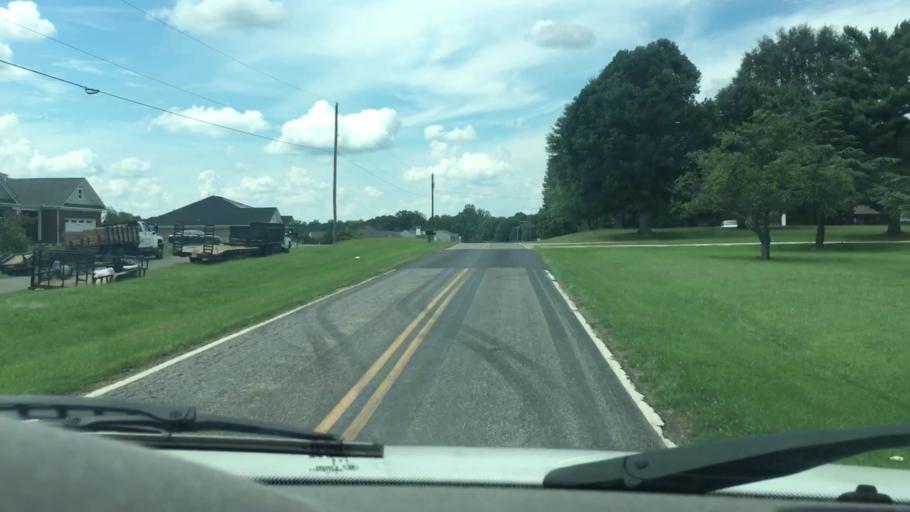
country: US
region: North Carolina
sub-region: Iredell County
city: Troutman
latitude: 35.6650
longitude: -80.8261
